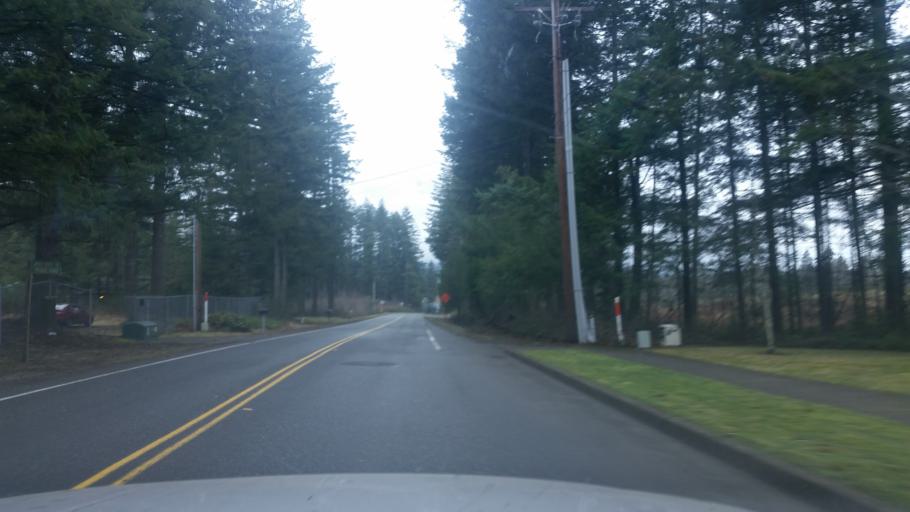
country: US
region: Washington
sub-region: King County
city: Tanner
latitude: 47.4743
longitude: -121.7371
